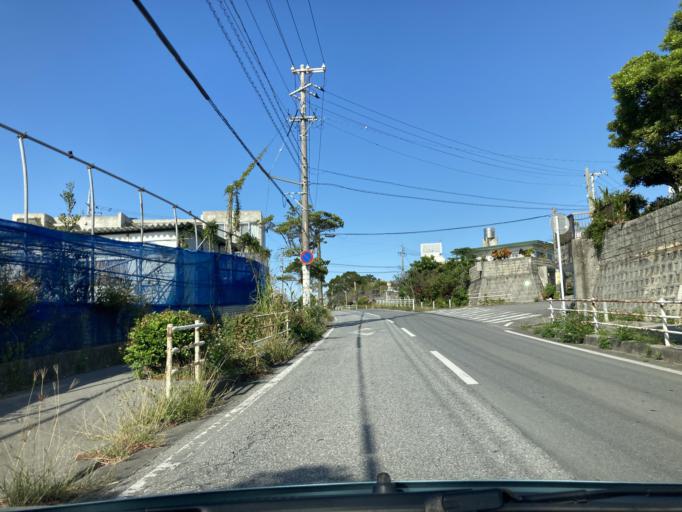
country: JP
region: Okinawa
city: Tomigusuku
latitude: 26.1772
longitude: 127.7059
